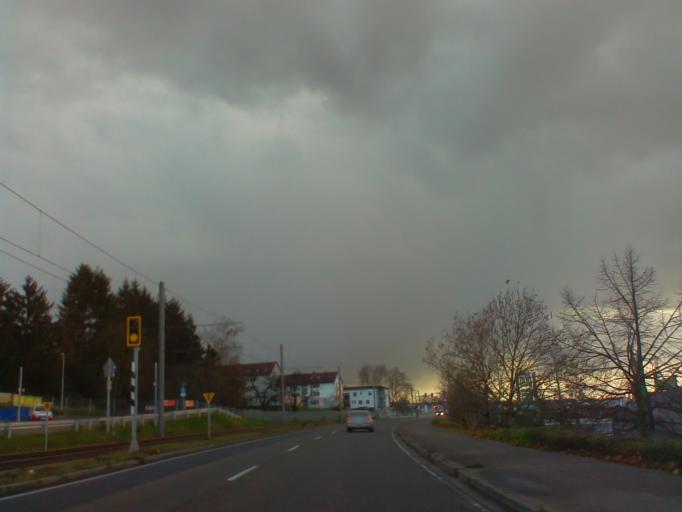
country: DE
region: Baden-Wuerttemberg
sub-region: Karlsruhe Region
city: Weinheim
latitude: 49.5354
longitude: 8.6592
